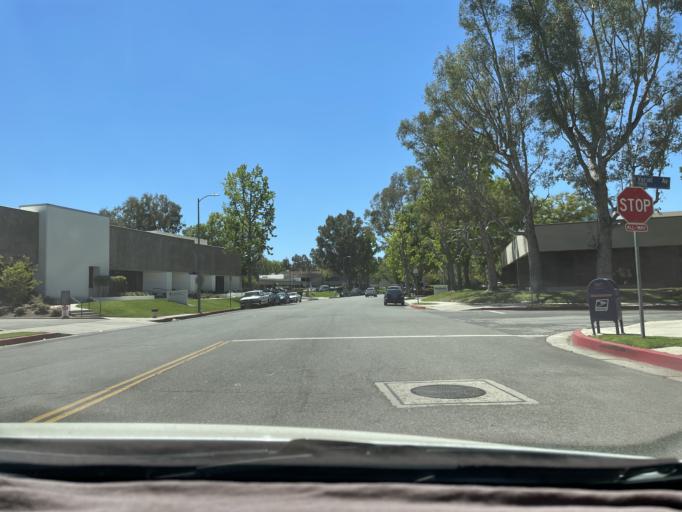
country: US
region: California
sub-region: Los Angeles County
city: Woodland Hills
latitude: 34.1772
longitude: -118.5920
